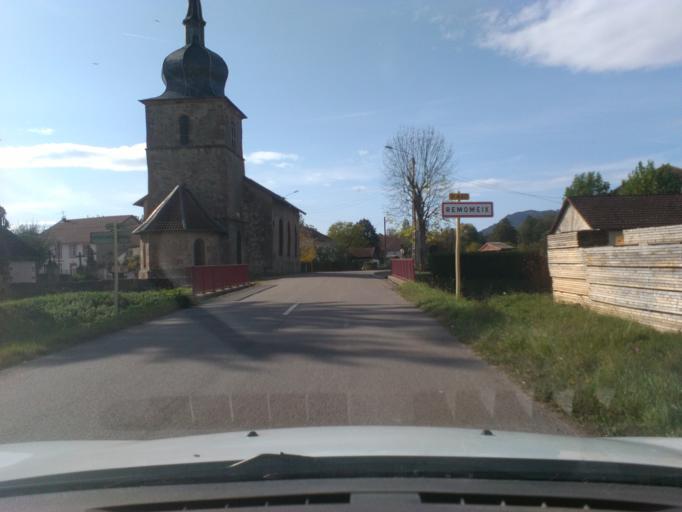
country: FR
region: Lorraine
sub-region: Departement des Vosges
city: Sainte-Marguerite
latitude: 48.2703
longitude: 7.0035
